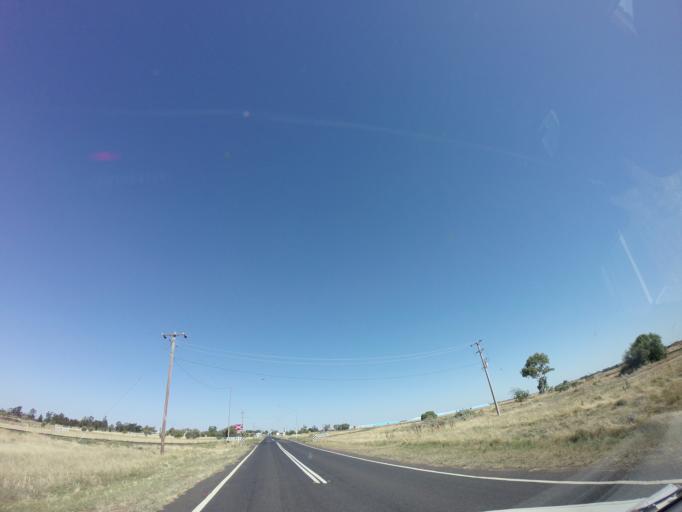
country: AU
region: New South Wales
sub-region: Bogan
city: Nyngan
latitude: -31.8343
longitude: 147.7112
